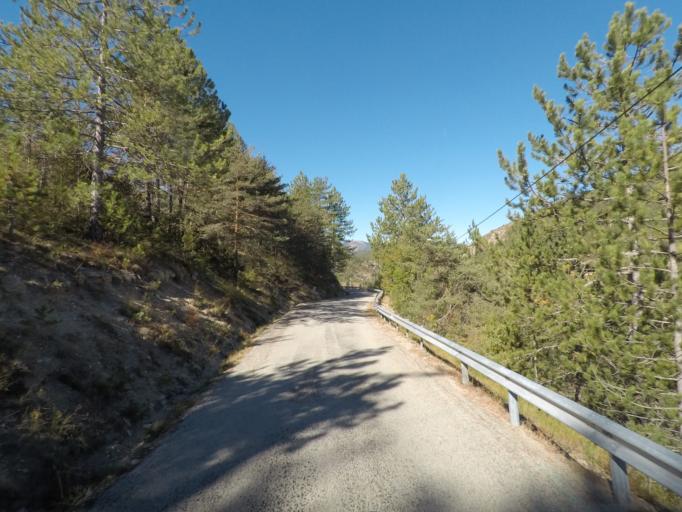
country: FR
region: Rhone-Alpes
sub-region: Departement de la Drome
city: Die
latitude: 44.5606
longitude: 5.3324
